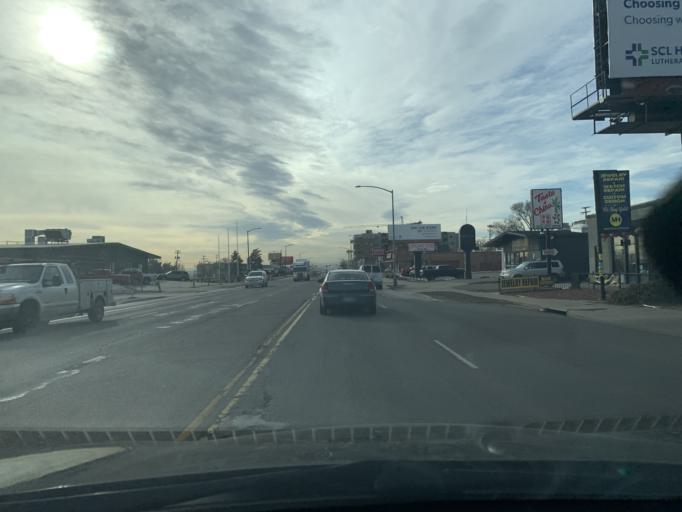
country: US
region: Colorado
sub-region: Jefferson County
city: Edgewater
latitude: 39.7473
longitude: -105.0253
